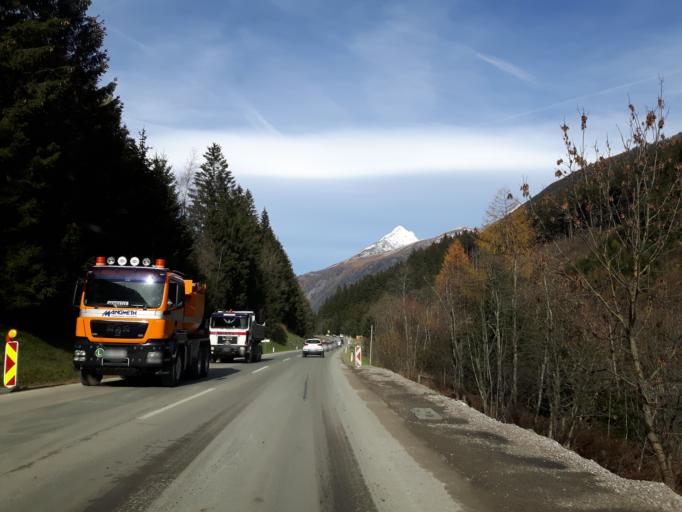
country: AT
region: Tyrol
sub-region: Politischer Bezirk Lienz
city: Matrei in Osttirol
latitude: 46.9636
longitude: 12.5517
